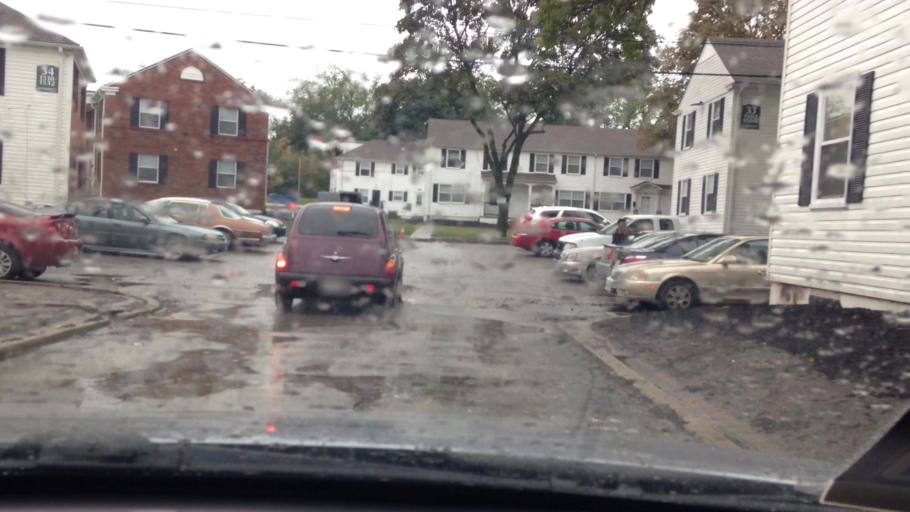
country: US
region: Kansas
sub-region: Johnson County
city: Westwood
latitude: 39.0432
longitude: -94.5669
